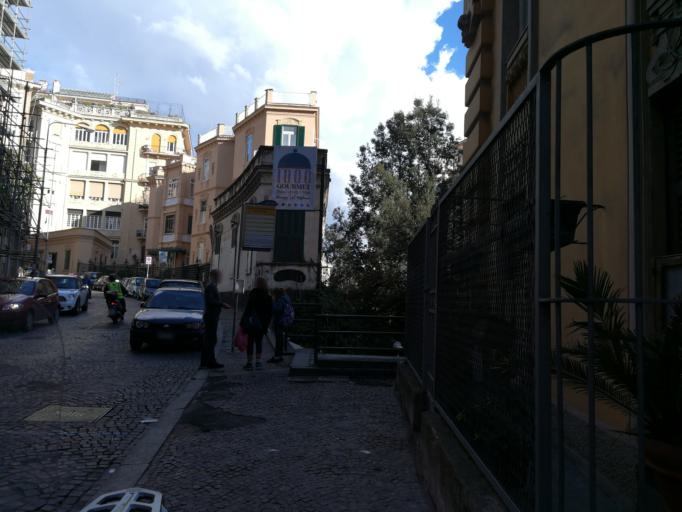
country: IT
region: Campania
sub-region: Provincia di Napoli
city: Napoli
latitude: 40.8375
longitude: 14.2363
